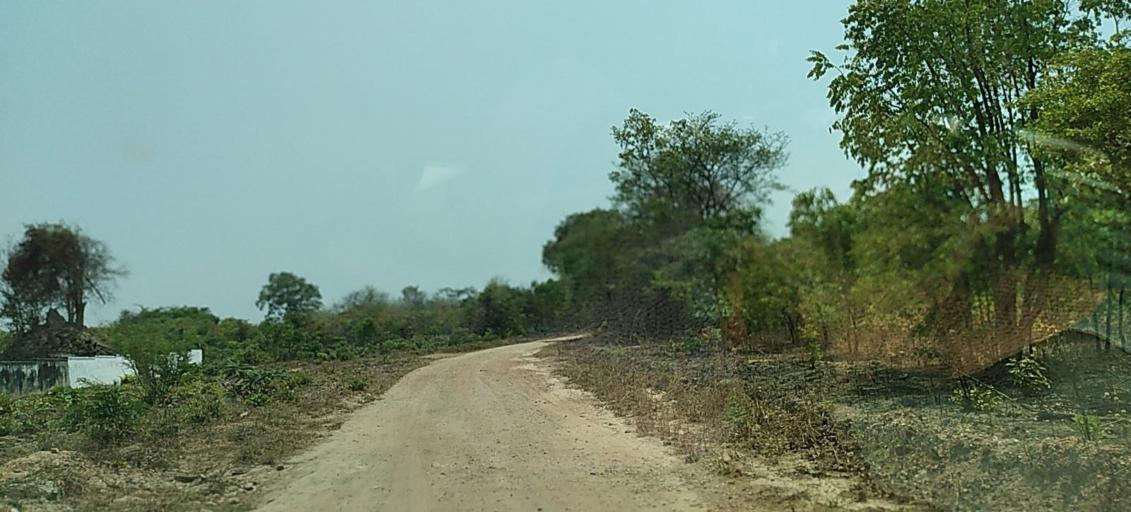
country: ZM
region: Copperbelt
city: Kalulushi
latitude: -12.9420
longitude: 28.1549
